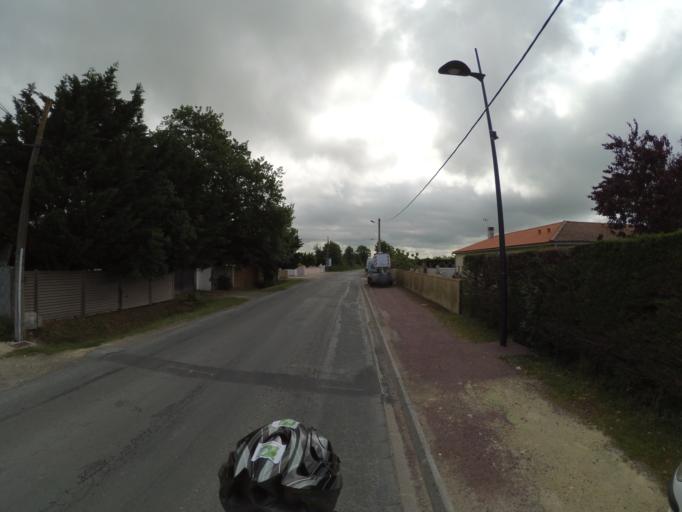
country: FR
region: Poitou-Charentes
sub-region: Departement de la Charente-Maritime
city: Chatelaillon-Plage
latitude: 46.0585
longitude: -1.0699
